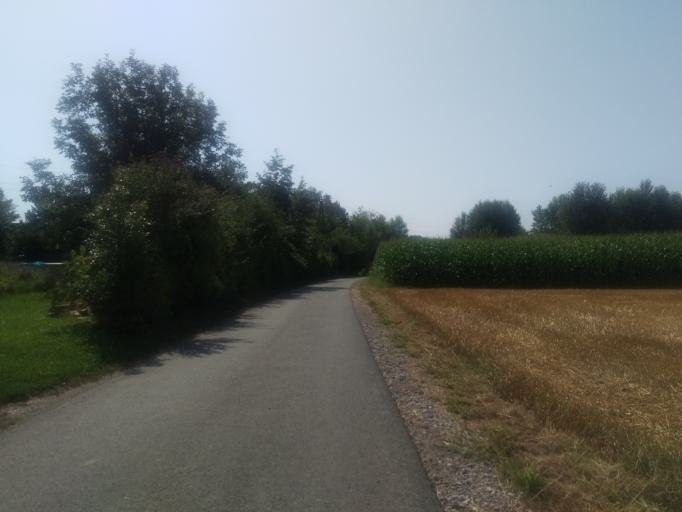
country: AT
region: Styria
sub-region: Politischer Bezirk Graz-Umgebung
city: Fernitz
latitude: 46.9754
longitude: 15.4942
